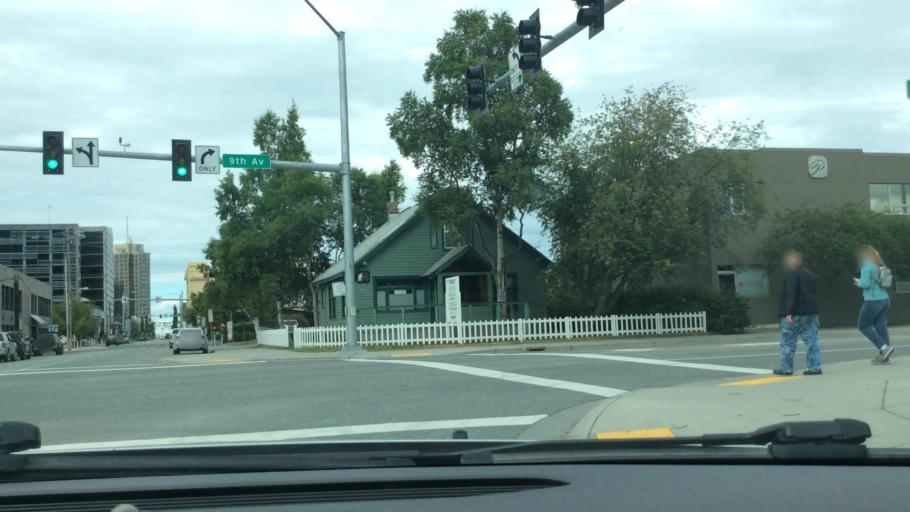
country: US
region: Alaska
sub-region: Anchorage Municipality
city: Anchorage
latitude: 61.2135
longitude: -149.8914
